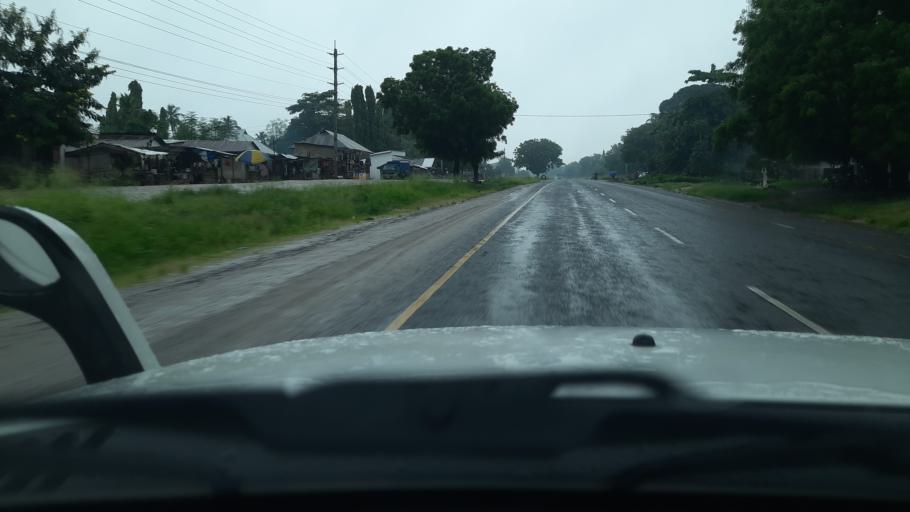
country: TZ
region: Pwani
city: Bagamoyo
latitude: -6.5115
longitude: 38.9405
